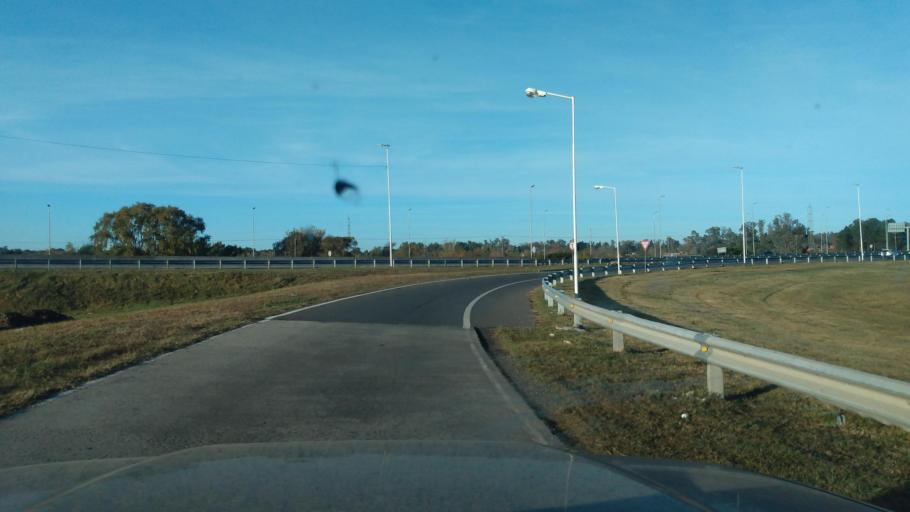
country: AR
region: Buenos Aires
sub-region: Partido de Lujan
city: Lujan
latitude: -34.5687
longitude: -59.0654
